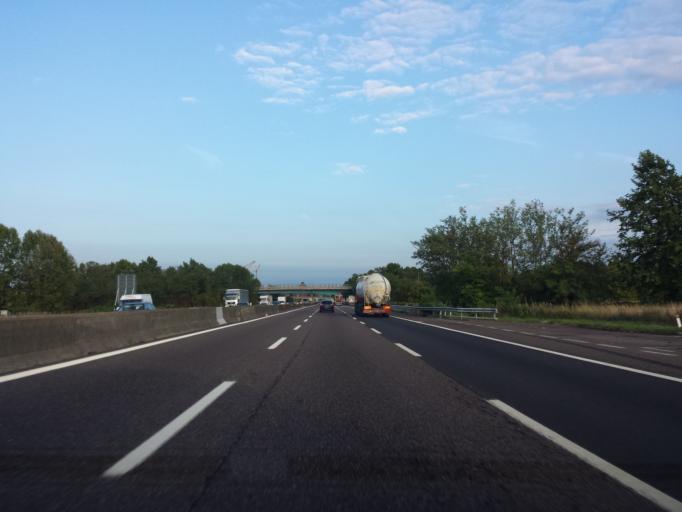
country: IT
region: Lombardy
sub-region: Provincia di Bergamo
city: Azzano San Paolo
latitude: 45.6684
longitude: 9.6790
